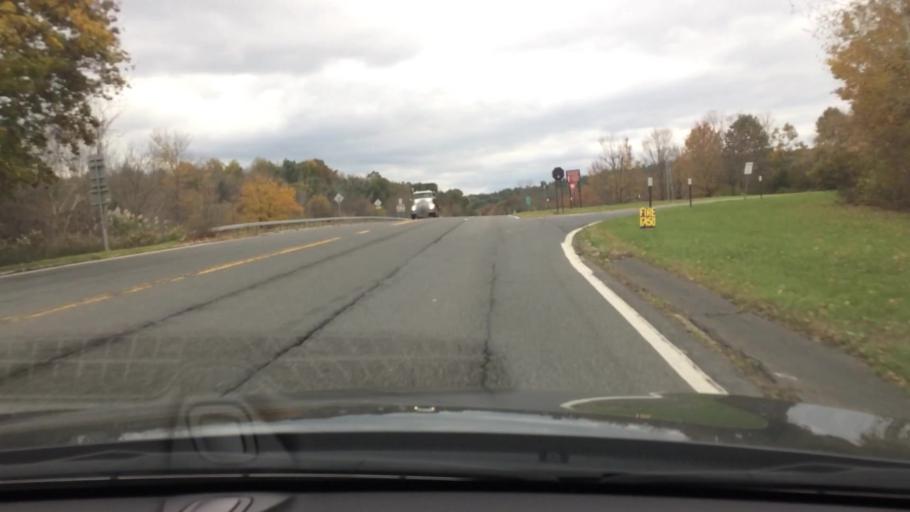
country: US
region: New York
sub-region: Columbia County
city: Philmont
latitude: 42.1191
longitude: -73.7163
